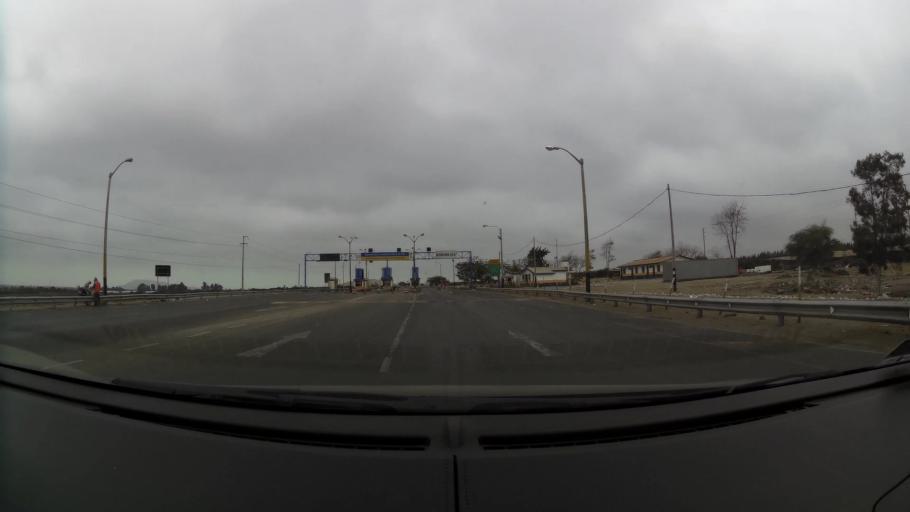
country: PE
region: La Libertad
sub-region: Viru
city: Viru
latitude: -8.4045
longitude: -78.8308
